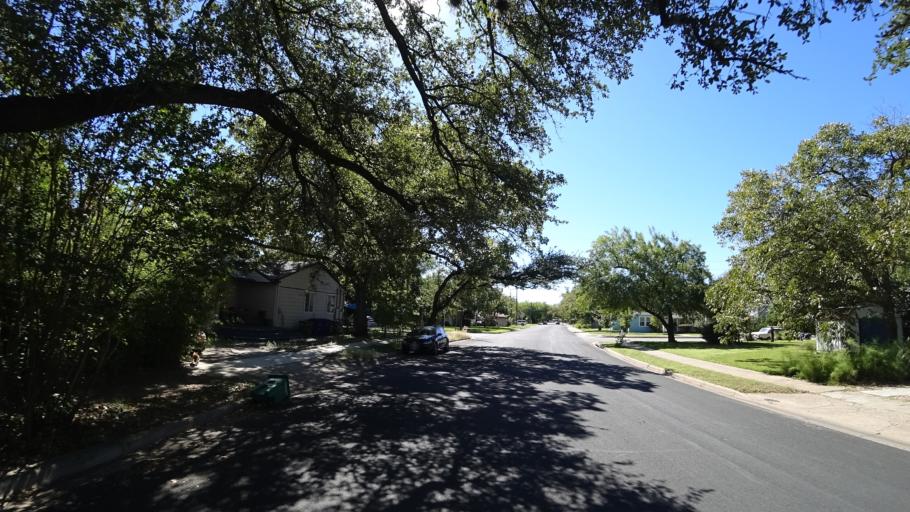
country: US
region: Texas
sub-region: Travis County
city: Austin
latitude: 30.3345
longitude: -97.7259
